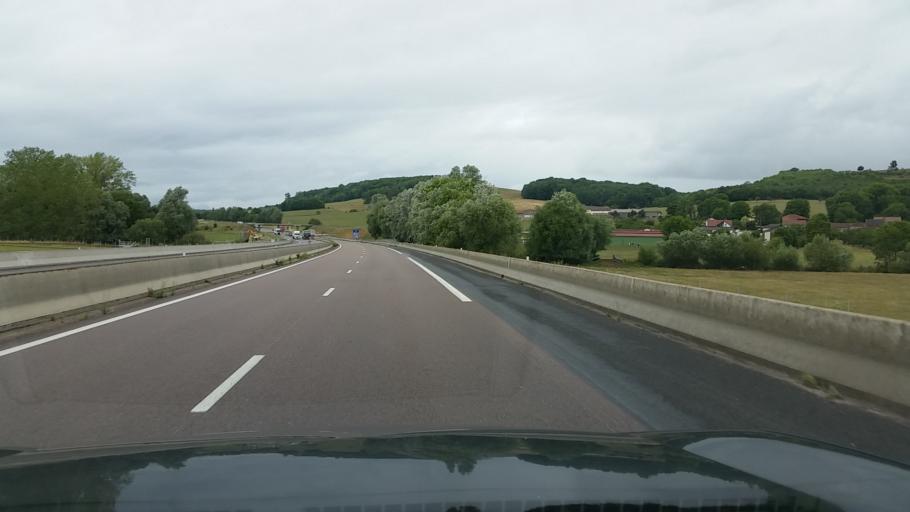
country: FR
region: Lorraine
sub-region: Departement des Vosges
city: Chatenois
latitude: 48.3249
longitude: 5.8564
